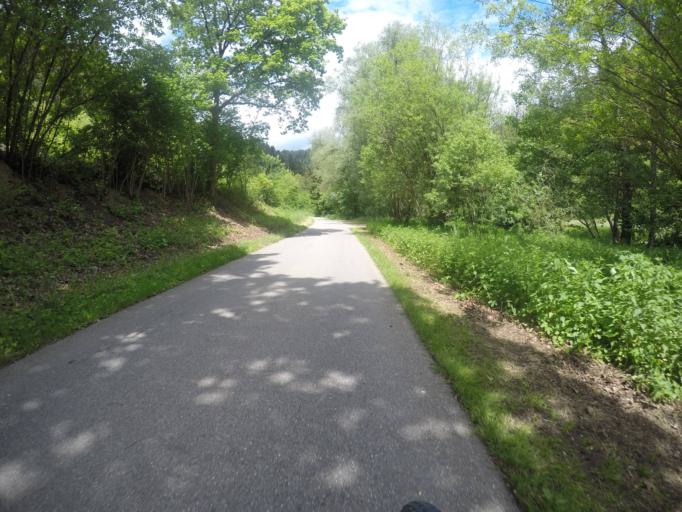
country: DE
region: Baden-Wuerttemberg
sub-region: Karlsruhe Region
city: Wildberg
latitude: 48.6396
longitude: 8.7449
